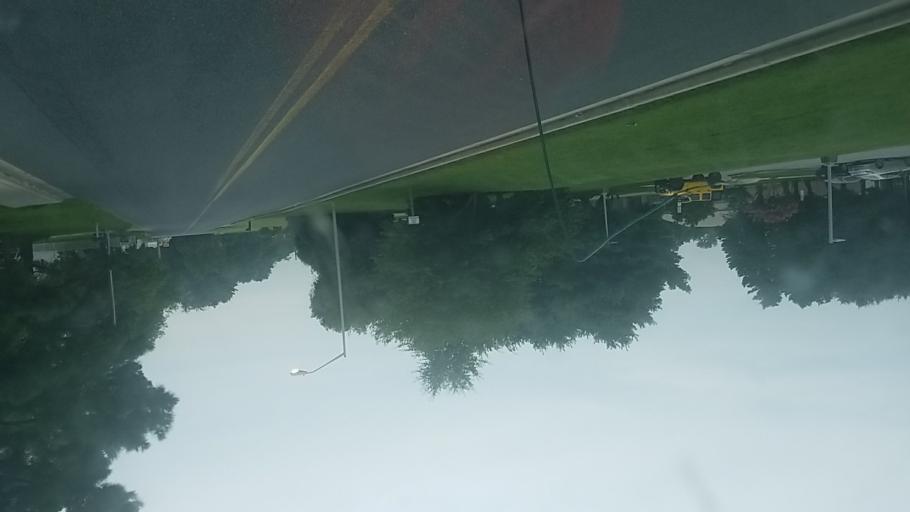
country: US
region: Maryland
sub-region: Wicomico County
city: Salisbury
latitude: 38.3693
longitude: -75.5475
